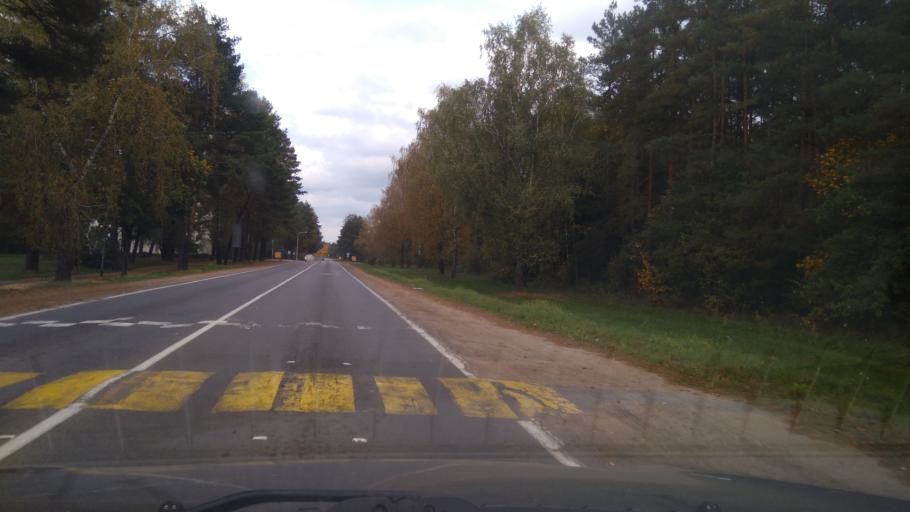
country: BY
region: Minsk
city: Svislach
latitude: 53.6472
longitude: 27.9197
